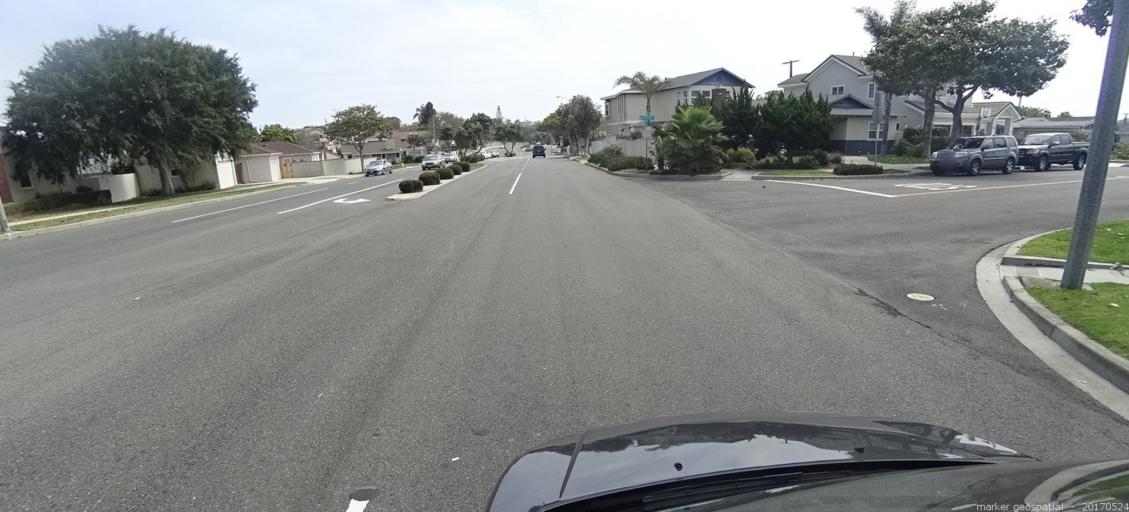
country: US
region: California
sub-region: Los Angeles County
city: Palos Verdes Estates
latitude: 33.8214
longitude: -118.3805
